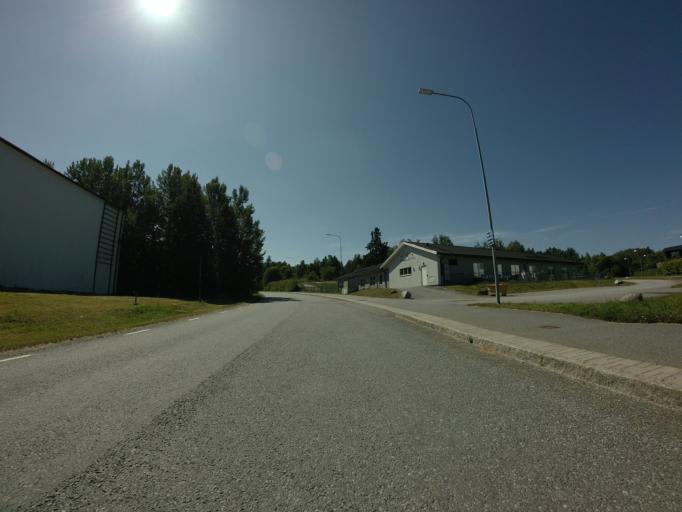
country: SE
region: Stockholm
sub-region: Lidingo
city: Brevik
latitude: 59.3597
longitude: 18.2236
